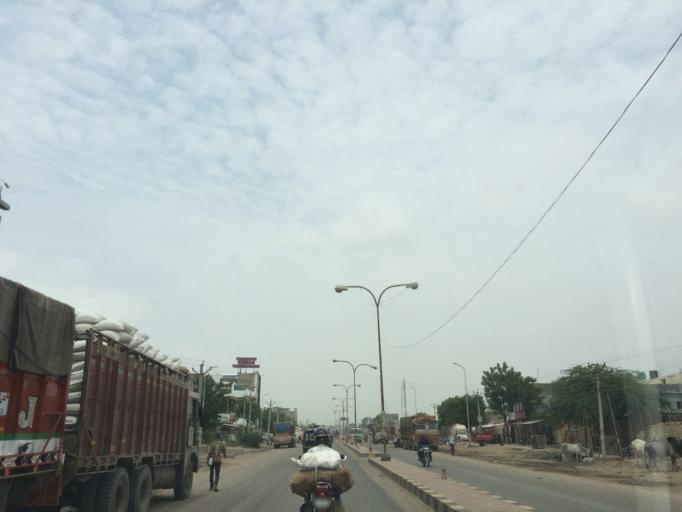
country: IN
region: Rajasthan
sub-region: Barmer
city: Barmer
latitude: 25.7558
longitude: 71.4148
